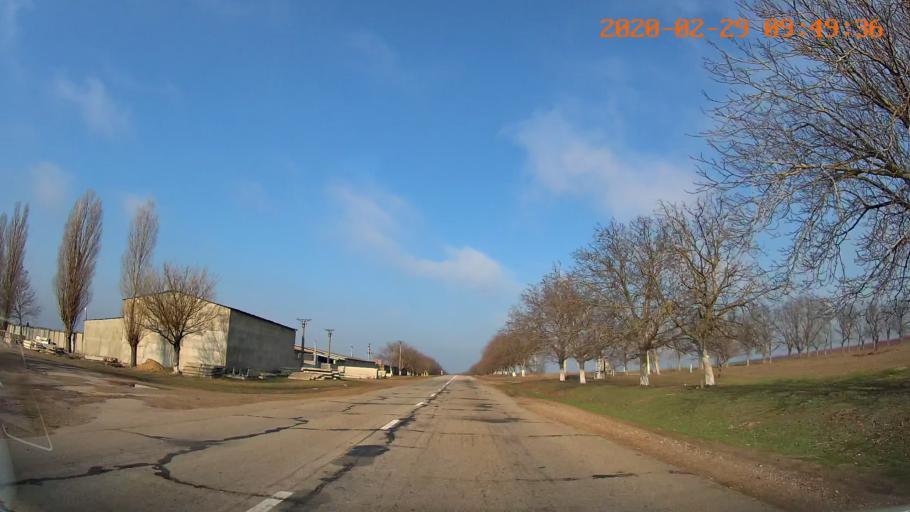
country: MD
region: Telenesti
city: Crasnoe
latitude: 46.6983
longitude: 29.7696
